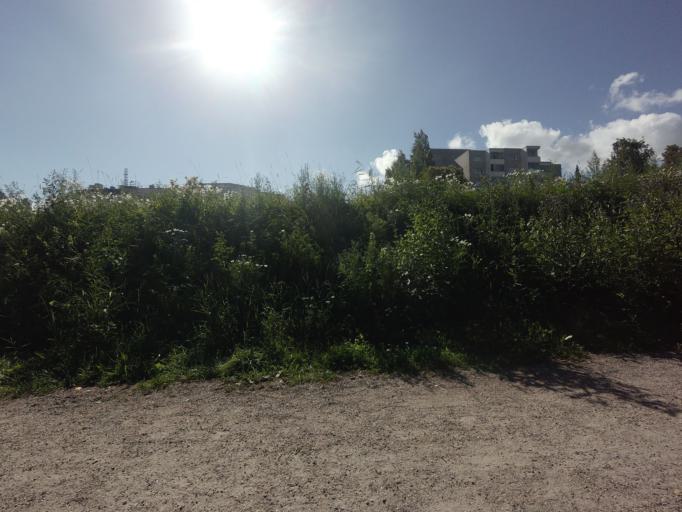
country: FI
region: Uusimaa
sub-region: Helsinki
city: Espoo
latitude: 60.1510
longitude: 24.6477
